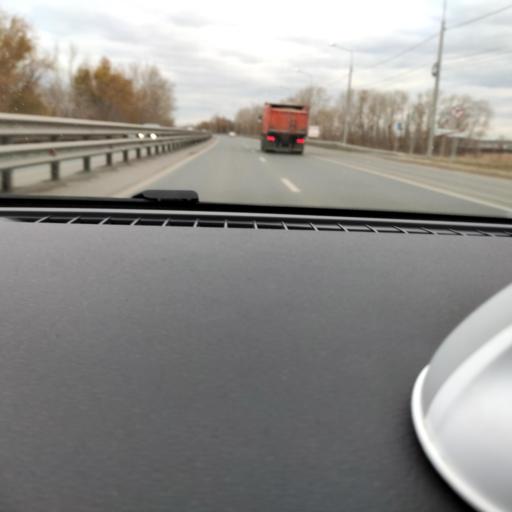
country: RU
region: Samara
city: Samara
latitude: 53.1011
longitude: 50.1613
